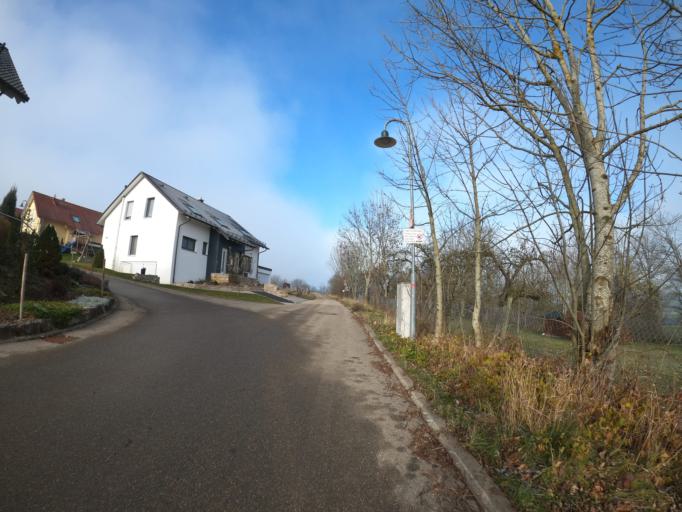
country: DE
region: Baden-Wuerttemberg
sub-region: Regierungsbezirk Stuttgart
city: Bad Uberkingen
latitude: 48.5873
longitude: 9.7583
